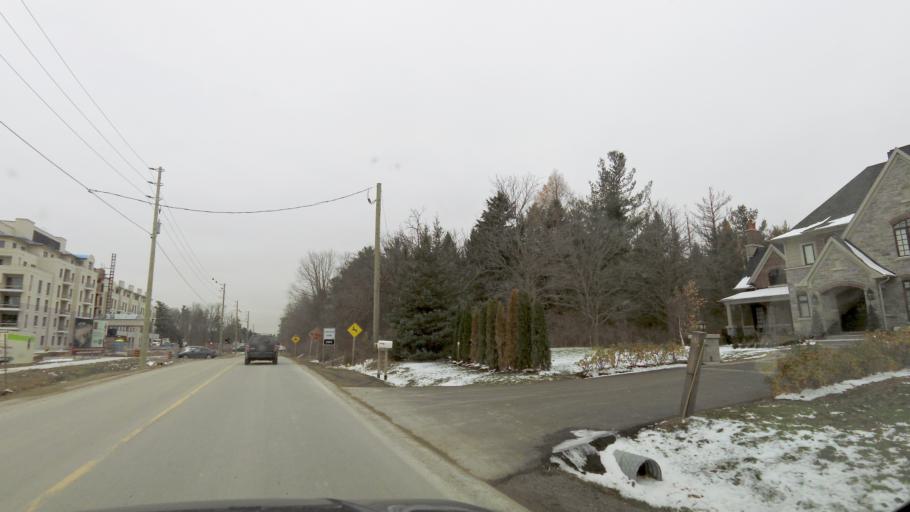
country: CA
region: Ontario
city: Vaughan
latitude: 43.8389
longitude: -79.5862
